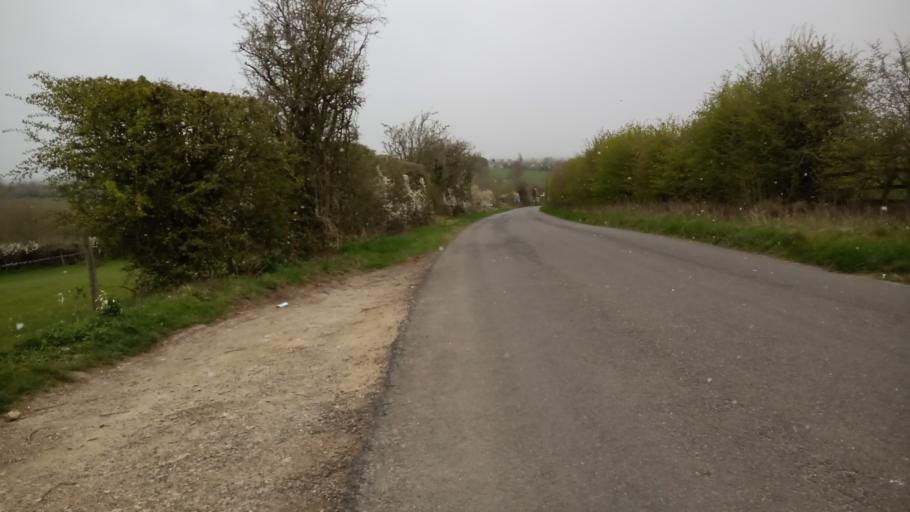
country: GB
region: England
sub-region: Oxfordshire
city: Witney
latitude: 51.8028
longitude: -1.5045
